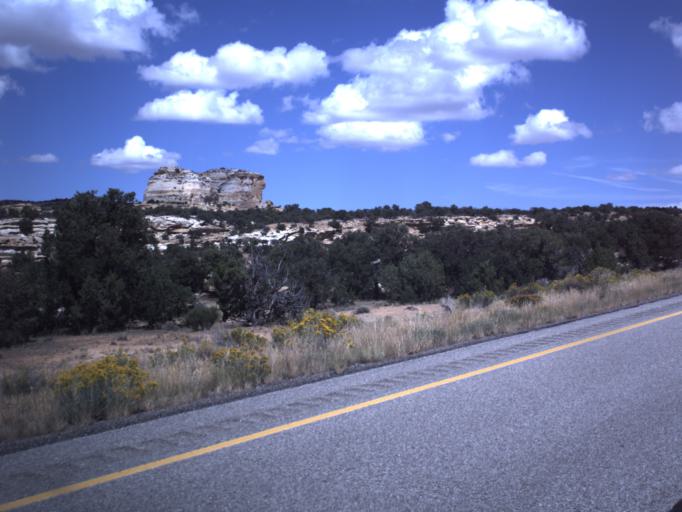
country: US
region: Utah
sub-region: Emery County
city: Ferron
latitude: 38.8625
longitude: -110.8591
